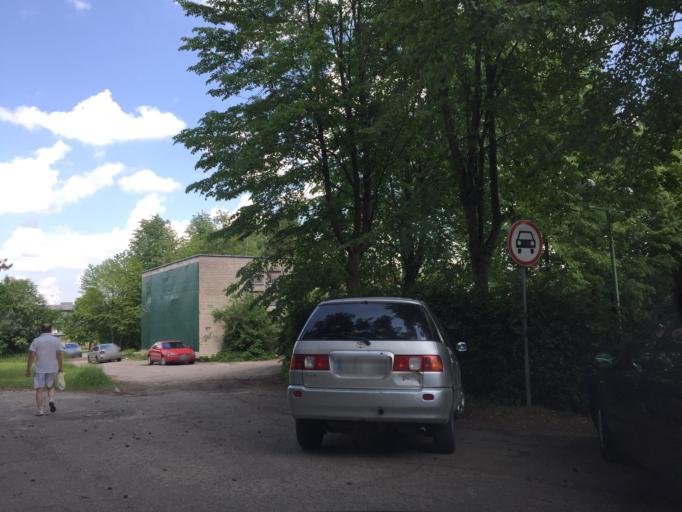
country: LT
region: Klaipedos apskritis
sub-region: Klaipeda
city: Palanga
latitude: 55.9283
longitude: 21.0635
